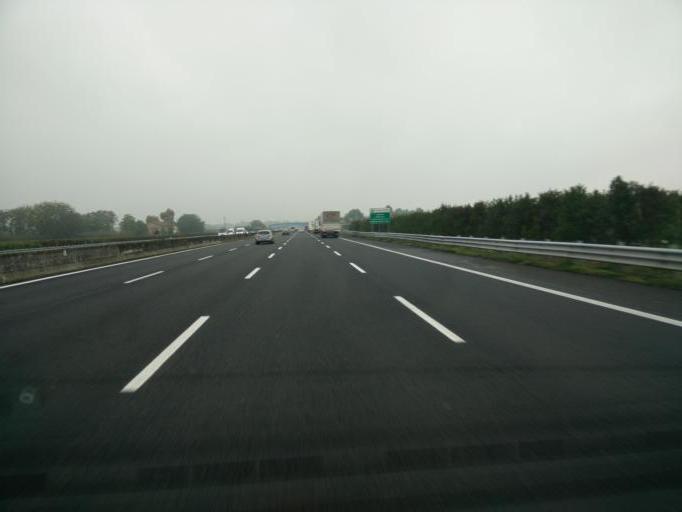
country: IT
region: Emilia-Romagna
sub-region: Provincia di Modena
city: San Cesario sul Panaro
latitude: 44.5725
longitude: 11.0079
